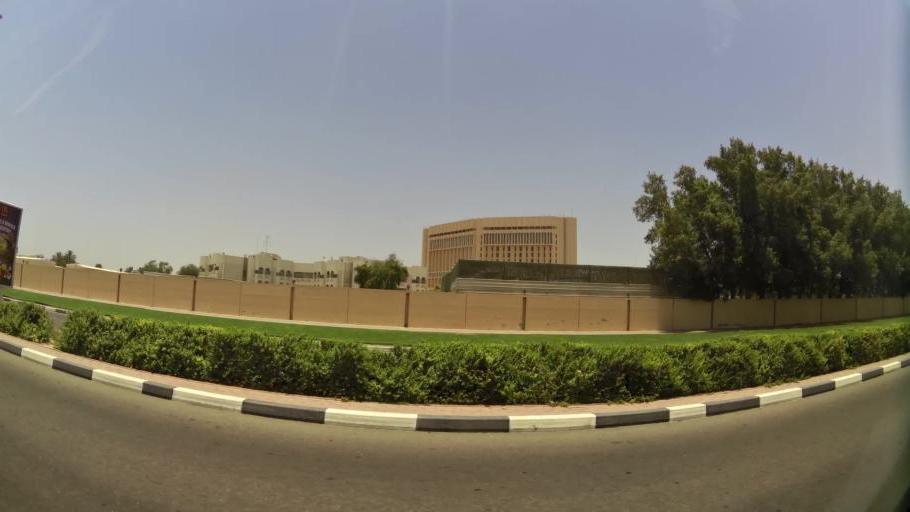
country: AE
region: Ash Shariqah
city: Sharjah
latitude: 25.2823
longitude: 55.3226
